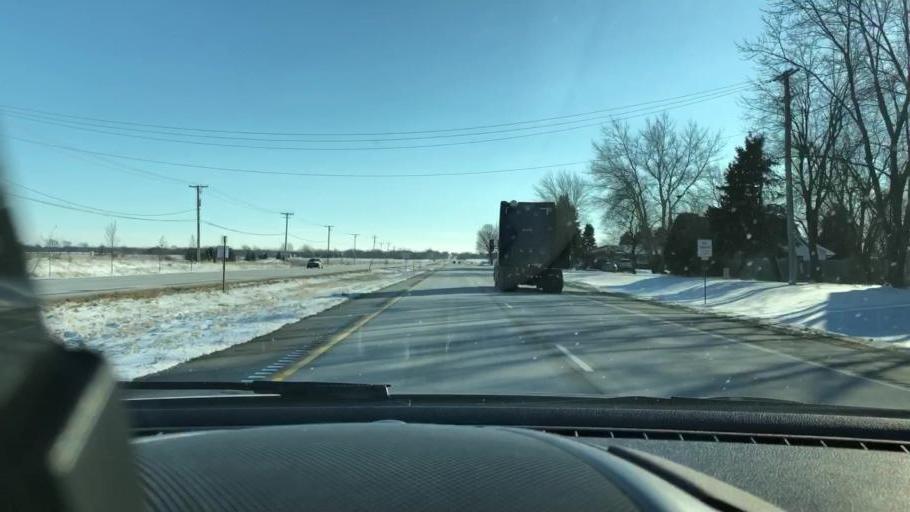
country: US
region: Illinois
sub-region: Will County
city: Preston Heights
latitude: 41.4503
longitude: -88.0792
